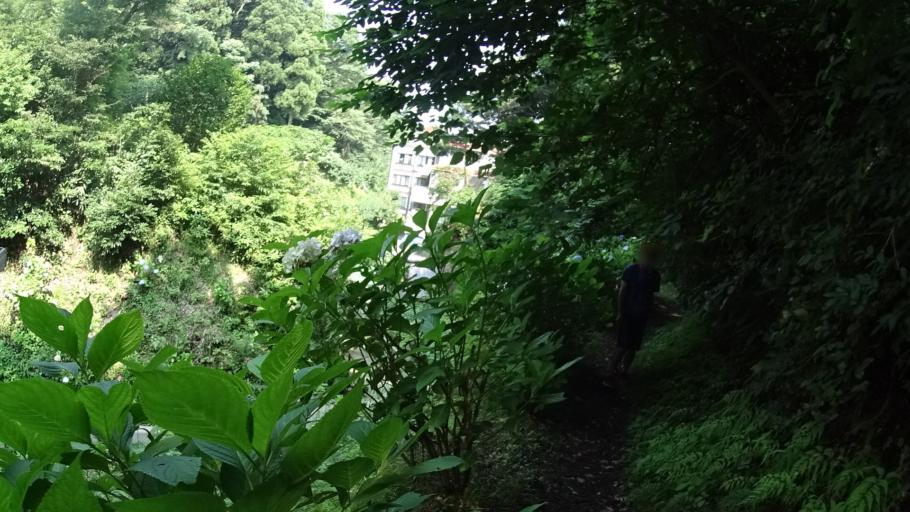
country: JP
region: Kanagawa
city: Zushi
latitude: 35.3055
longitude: 139.6034
